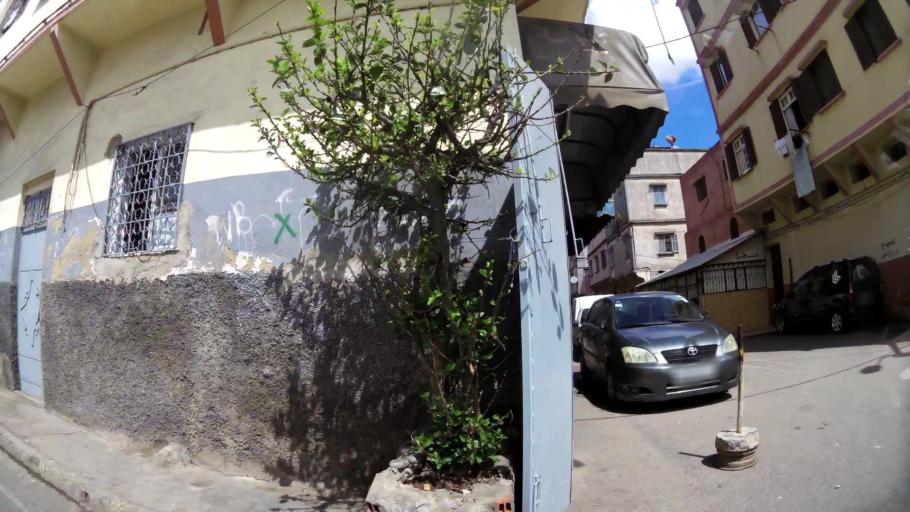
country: MA
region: Grand Casablanca
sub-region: Casablanca
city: Casablanca
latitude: 33.5578
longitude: -7.6038
